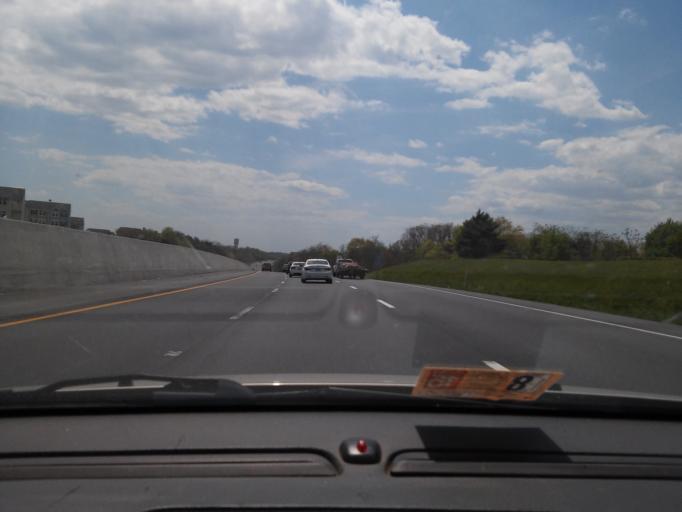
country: US
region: Maryland
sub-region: Washington County
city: Williamsport
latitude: 39.5776
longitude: -77.8814
